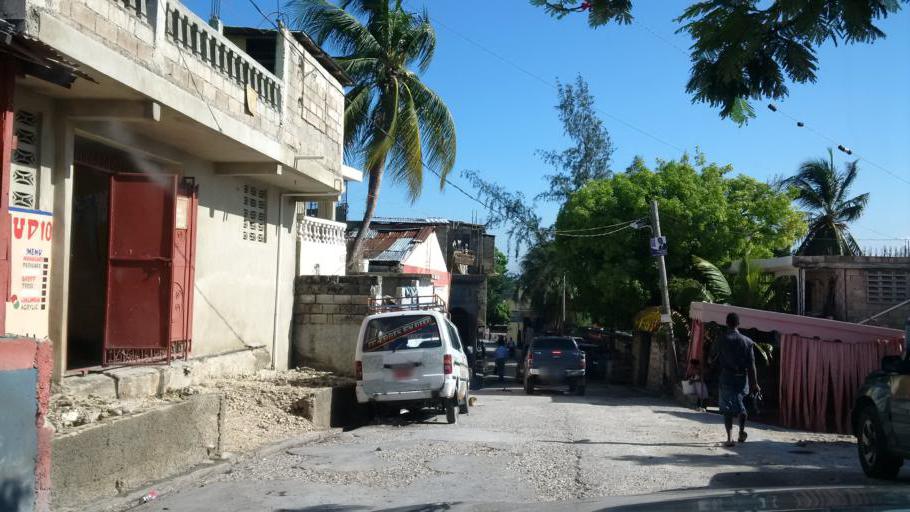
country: HT
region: Ouest
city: Delmas 73
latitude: 18.5474
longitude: -72.3125
